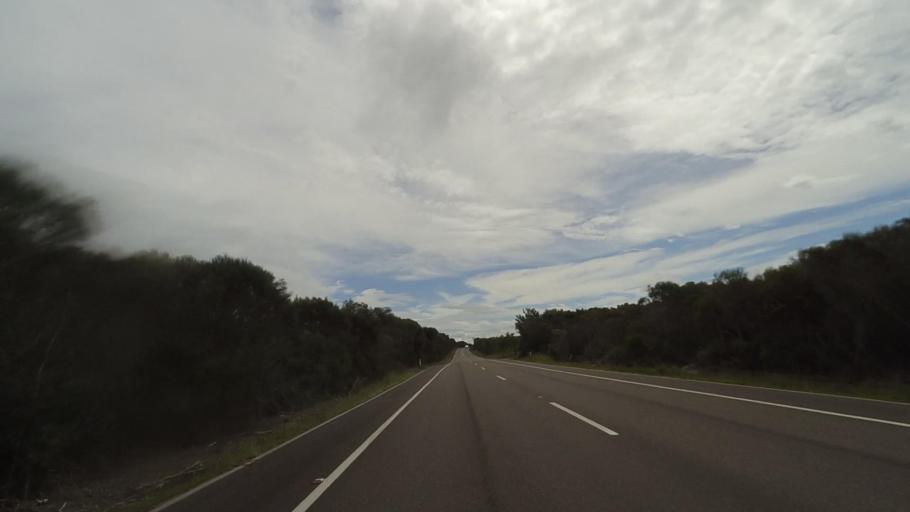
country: AU
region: New South Wales
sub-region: Sutherland Shire
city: Dolans Bay
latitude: -34.1029
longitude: 151.1164
